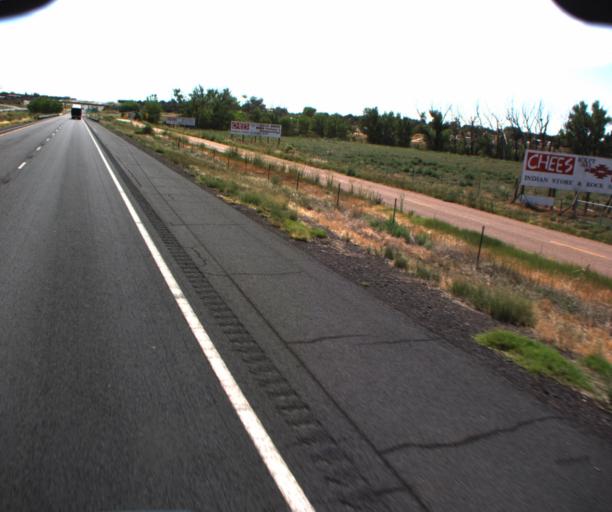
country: US
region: Arizona
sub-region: Apache County
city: Houck
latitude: 35.2827
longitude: -109.2192
